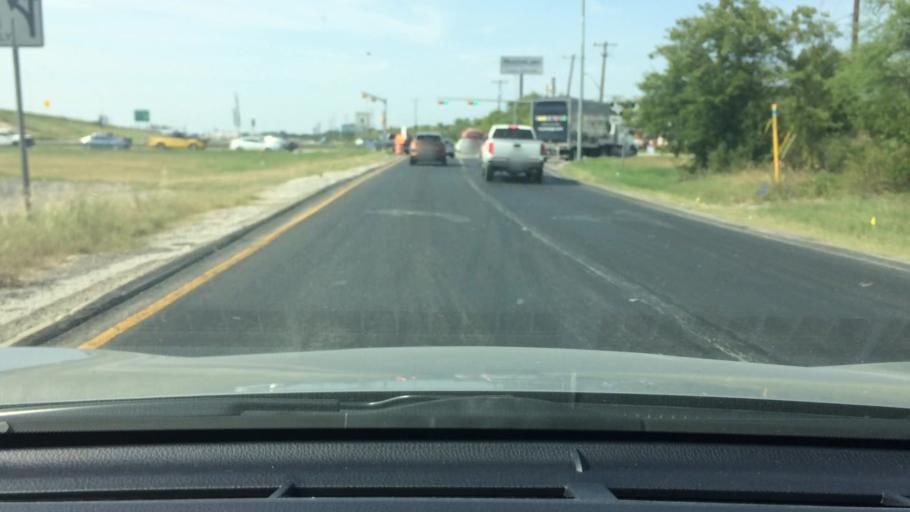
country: US
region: Texas
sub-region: Bexar County
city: Kirby
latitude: 29.4224
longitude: -98.3886
